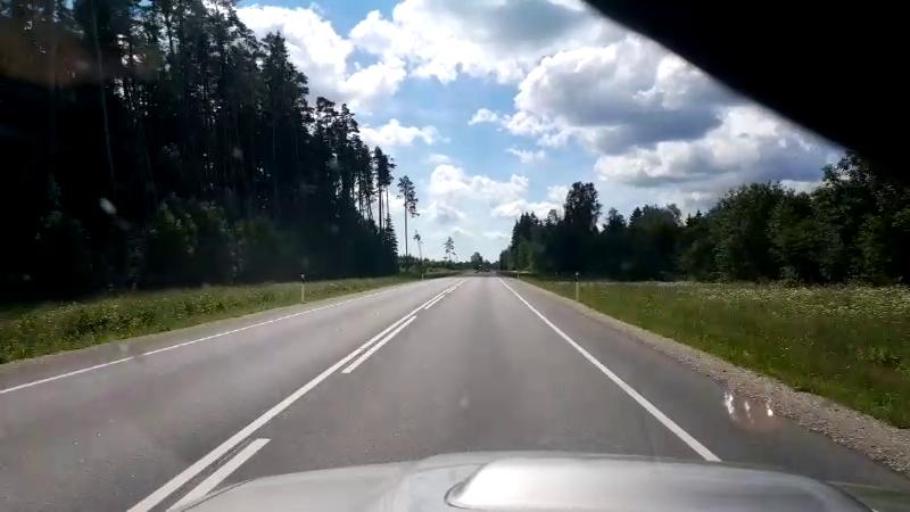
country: EE
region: Jaervamaa
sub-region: Jaerva-Jaani vald
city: Jarva-Jaani
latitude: 59.0477
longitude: 25.7071
